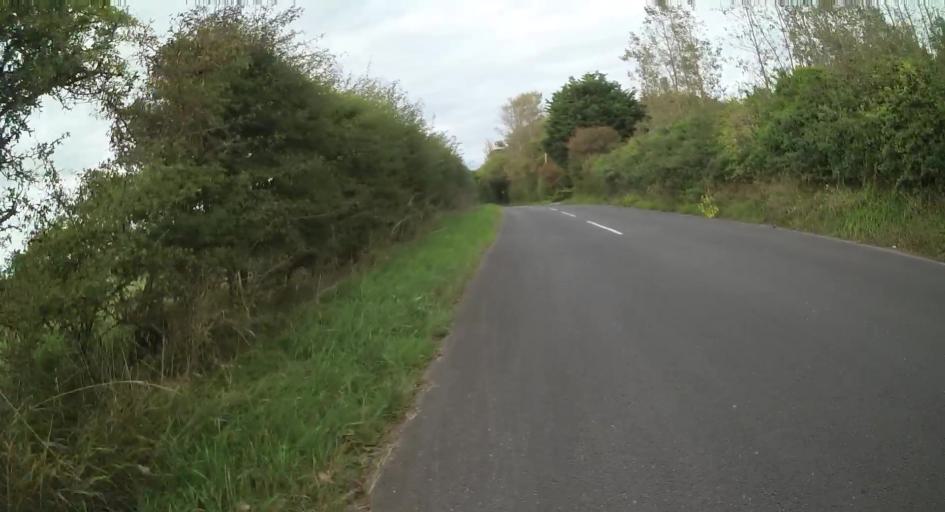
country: GB
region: England
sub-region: Isle of Wight
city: Freshwater
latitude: 50.6798
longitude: -1.4960
